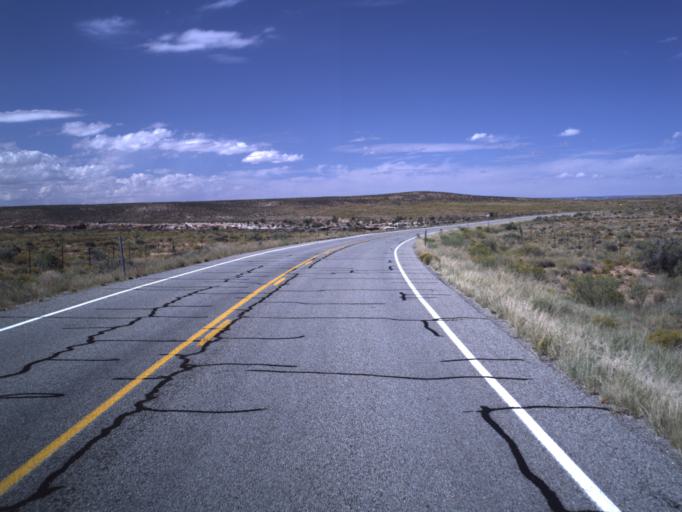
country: US
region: Utah
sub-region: San Juan County
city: Blanding
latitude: 37.2915
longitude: -109.4158
